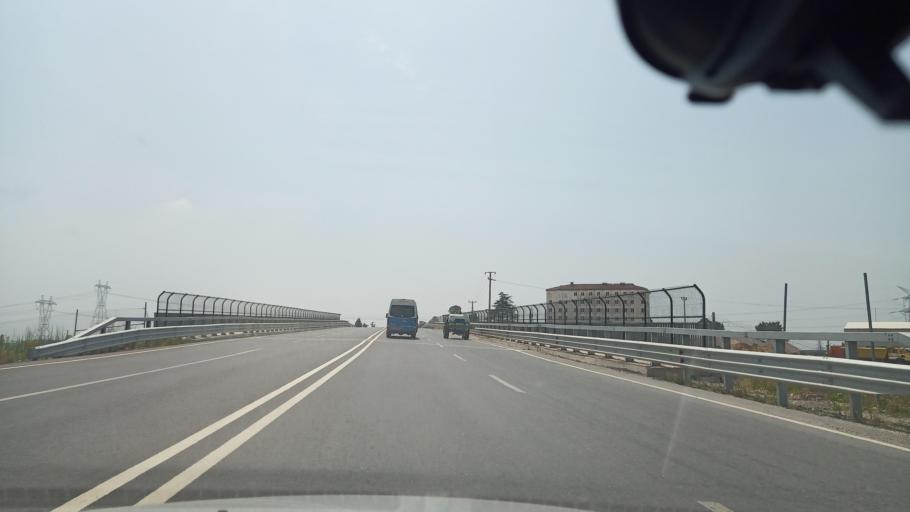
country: TR
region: Sakarya
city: Adapazari
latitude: 40.8255
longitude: 30.3966
